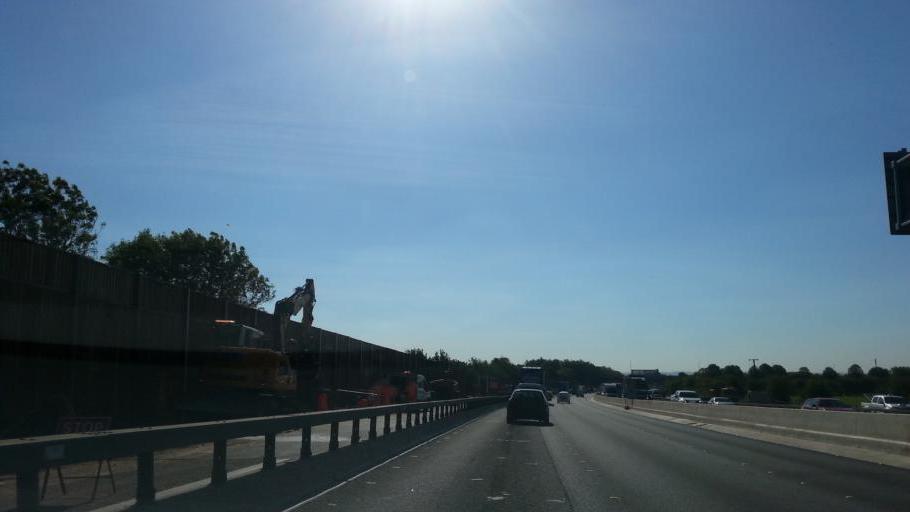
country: GB
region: England
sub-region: Derbyshire
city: Long Eaton
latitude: 52.9029
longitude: -1.2991
